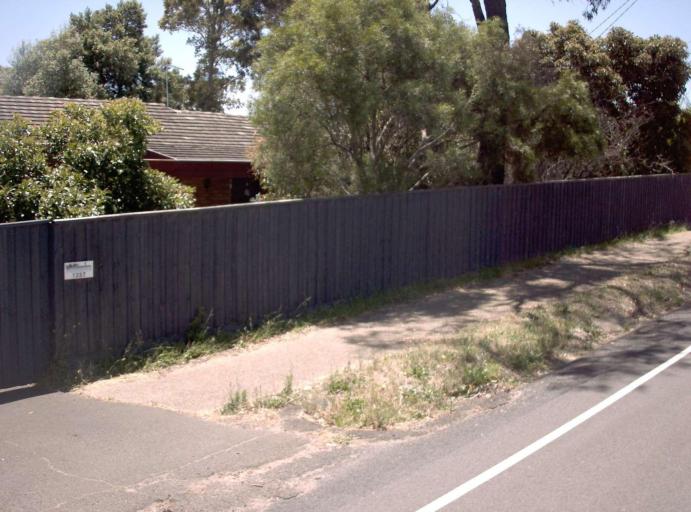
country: AU
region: Victoria
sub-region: Mornington Peninsula
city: Mount Eliza
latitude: -38.2026
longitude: 145.0793
